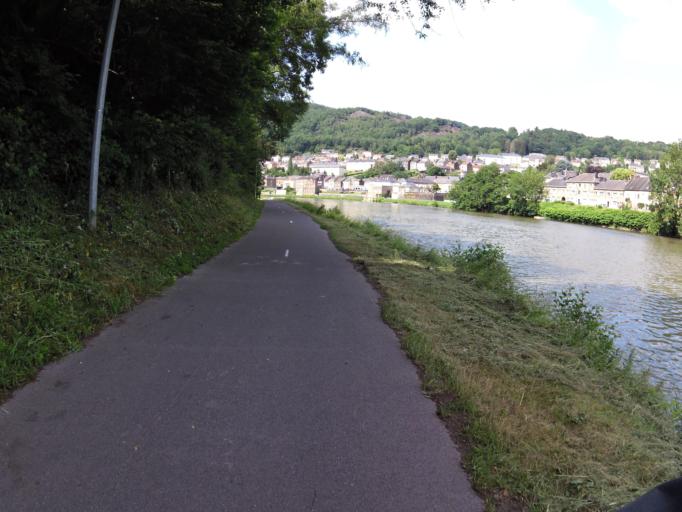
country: FR
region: Champagne-Ardenne
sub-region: Departement des Ardennes
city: Montherme
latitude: 49.8829
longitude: 4.7371
